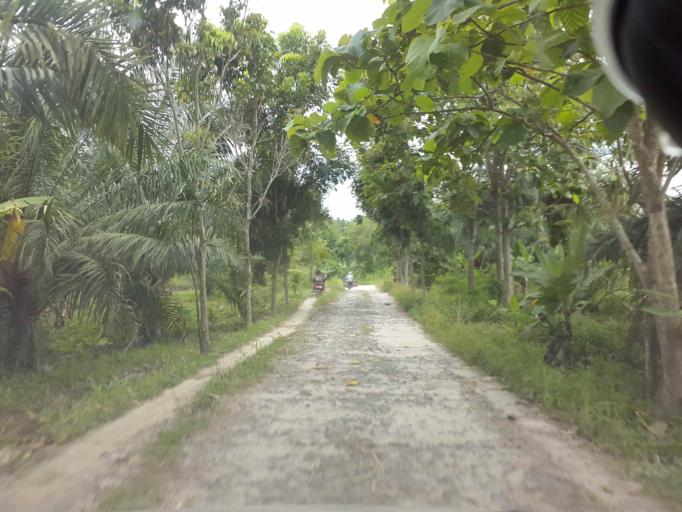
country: ID
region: Lampung
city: Palas
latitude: -5.6674
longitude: 105.7447
